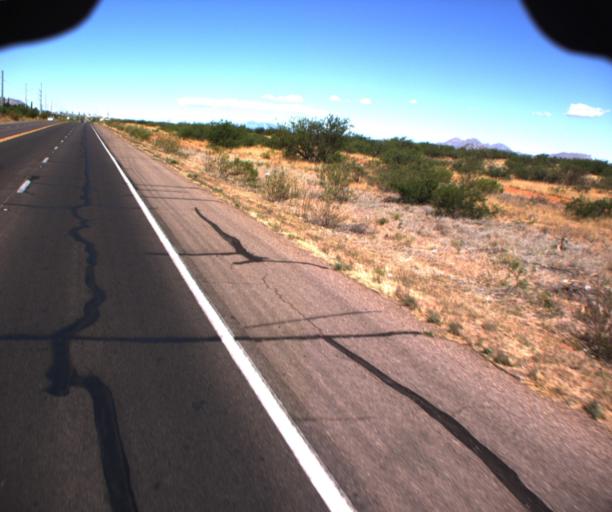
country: US
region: Arizona
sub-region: Cochise County
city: Sierra Vista
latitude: 31.5695
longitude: -110.2865
